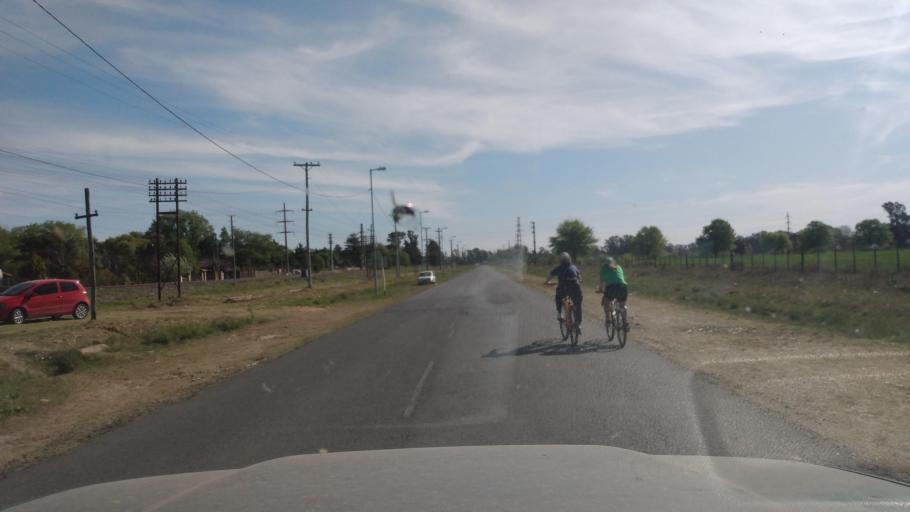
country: AR
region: Buenos Aires
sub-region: Partido de Lujan
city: Lujan
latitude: -34.5878
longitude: -59.1359
